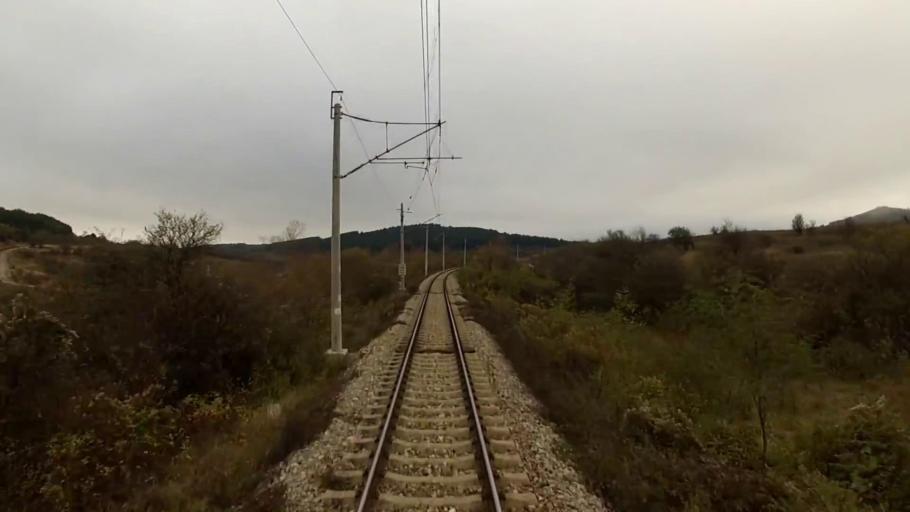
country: BG
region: Sofiya
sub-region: Obshtina Dragoman
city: Dragoman
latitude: 42.9390
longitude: 22.9023
